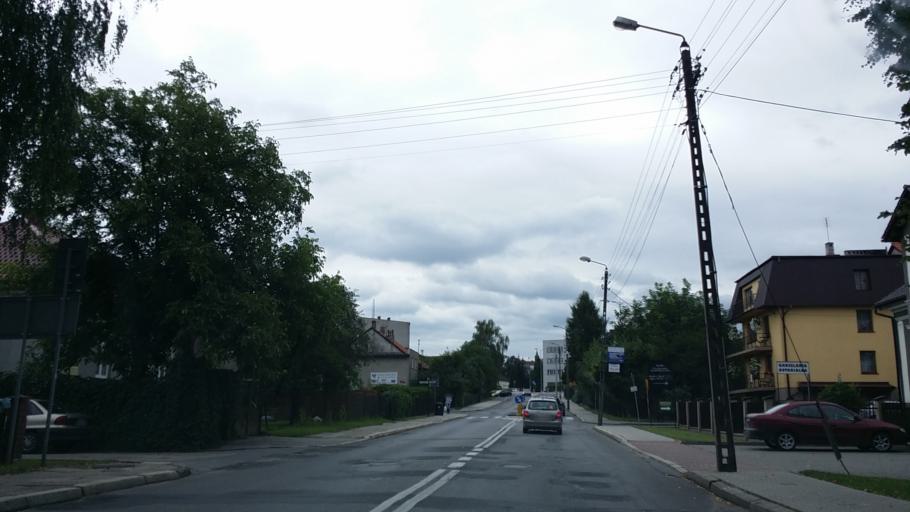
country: PL
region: Lesser Poland Voivodeship
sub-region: Powiat wadowicki
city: Wadowice
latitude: 49.8854
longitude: 19.4846
